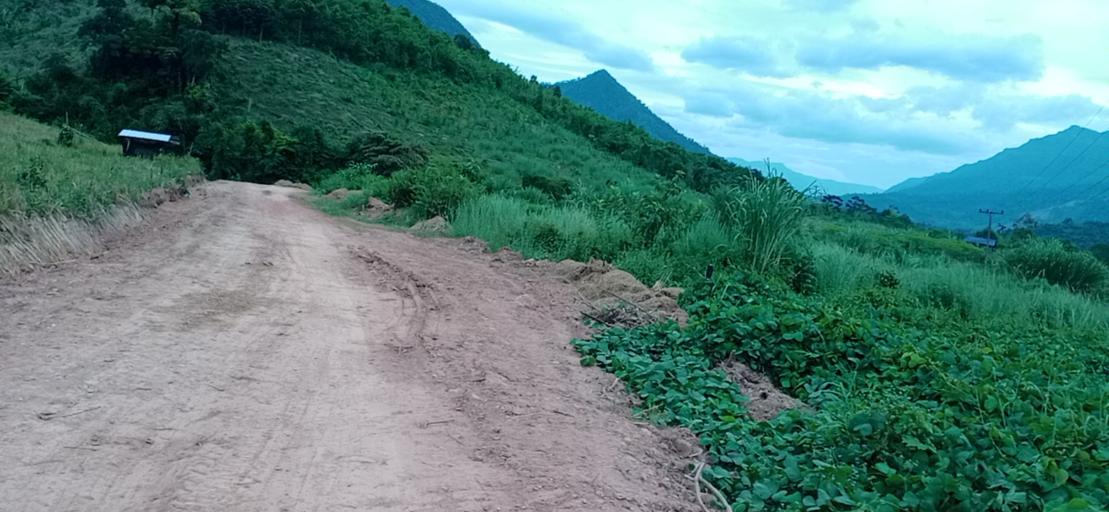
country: TH
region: Changwat Bueng Kan
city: Pak Khat
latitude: 18.5523
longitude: 103.1638
